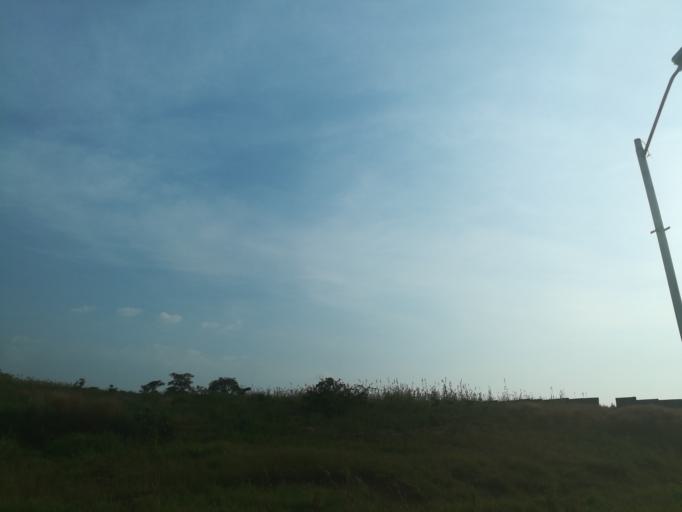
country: NG
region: Abuja Federal Capital Territory
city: Abuja
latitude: 9.0909
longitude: 7.3717
